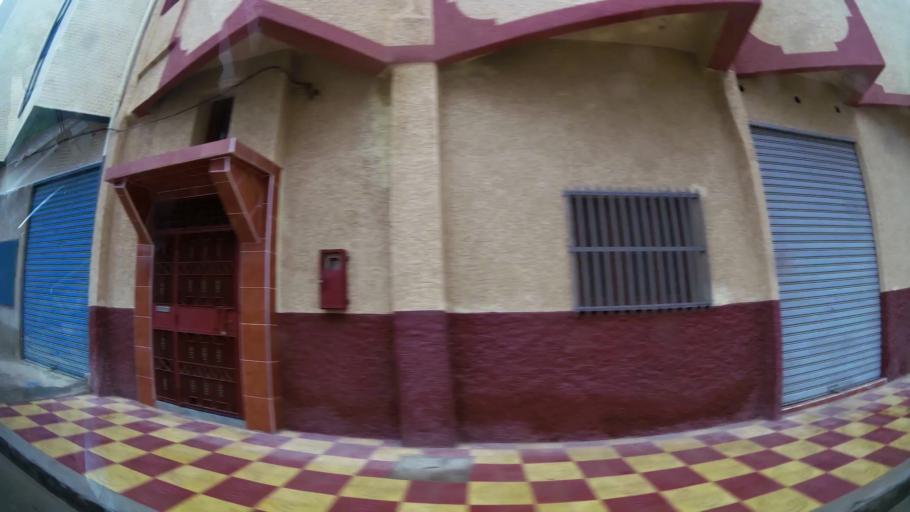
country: MA
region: Taza-Al Hoceima-Taounate
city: Imzourene
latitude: 35.1396
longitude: -3.8487
